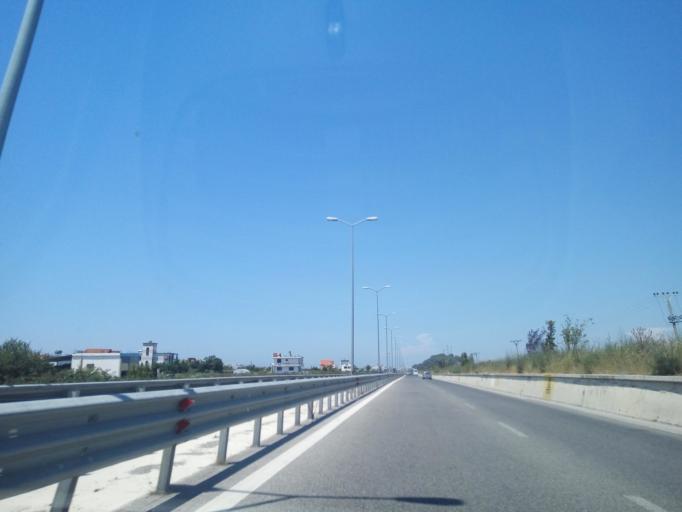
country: AL
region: Tirane
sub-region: Rrethi i Tiranes
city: Shengjergj
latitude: 41.2142
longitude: 19.5316
